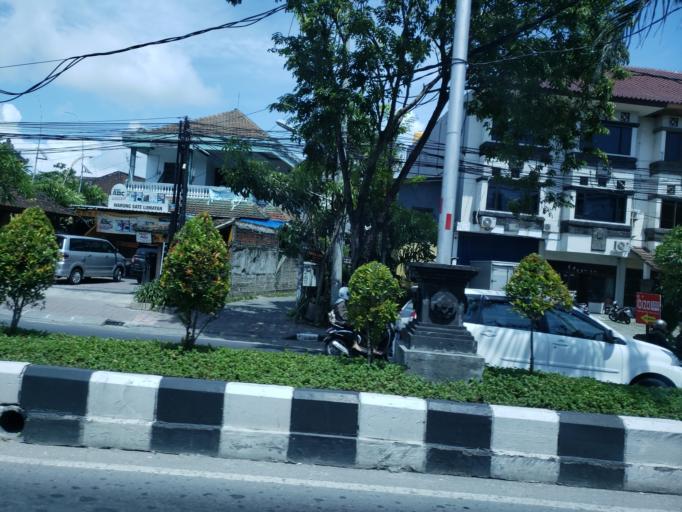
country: ID
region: Bali
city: Kelanabian
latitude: -8.7408
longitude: 115.1805
